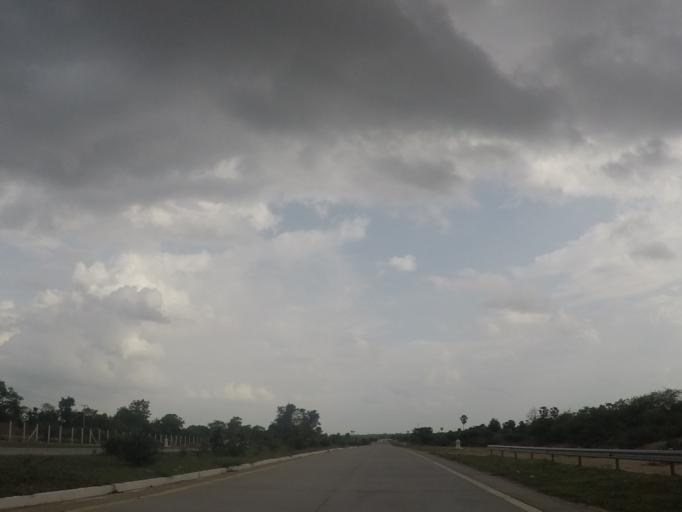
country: MM
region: Mandalay
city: Meiktila
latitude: 20.8021
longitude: 95.7694
